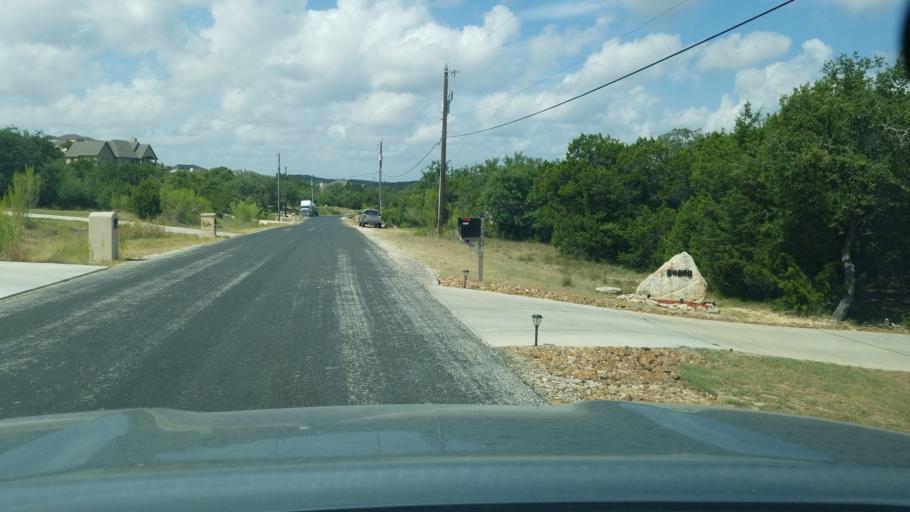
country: US
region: Texas
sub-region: Bexar County
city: Timberwood Park
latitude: 29.6806
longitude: -98.5181
